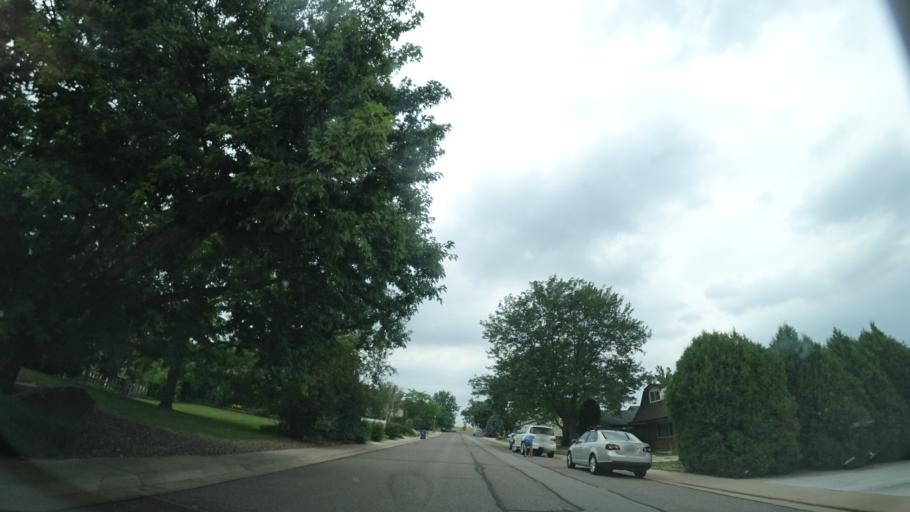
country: US
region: Colorado
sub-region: Jefferson County
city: West Pleasant View
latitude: 39.7074
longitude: -105.1570
